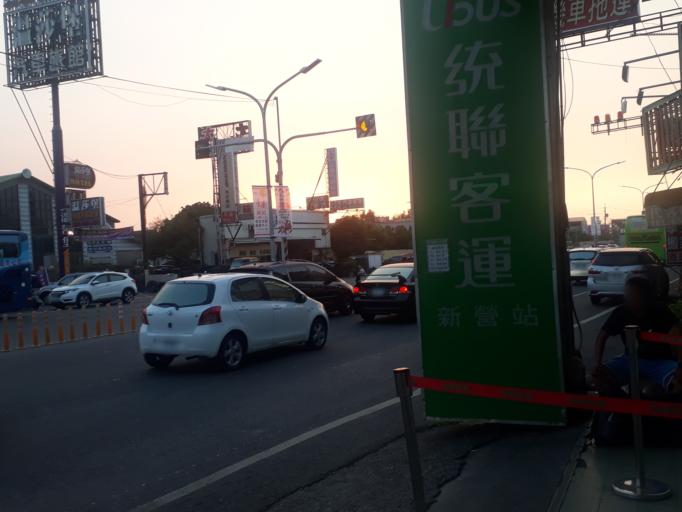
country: TW
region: Taiwan
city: Xinying
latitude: 23.3061
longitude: 120.2957
